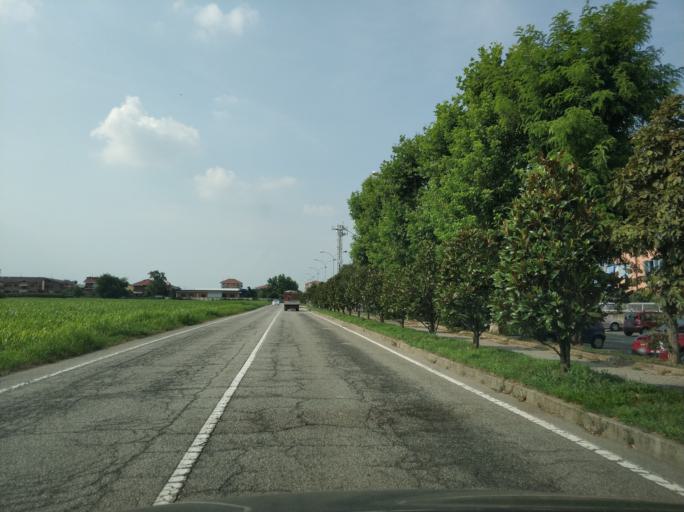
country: IT
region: Piedmont
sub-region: Provincia di Torino
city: Leini
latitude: 45.1780
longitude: 7.7095
